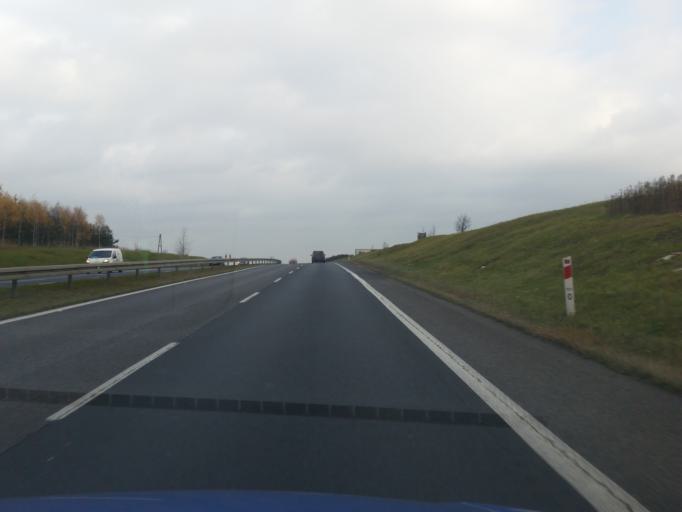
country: PL
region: Silesian Voivodeship
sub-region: Powiat myszkowski
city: Kozieglowy
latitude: 50.5808
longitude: 19.1639
